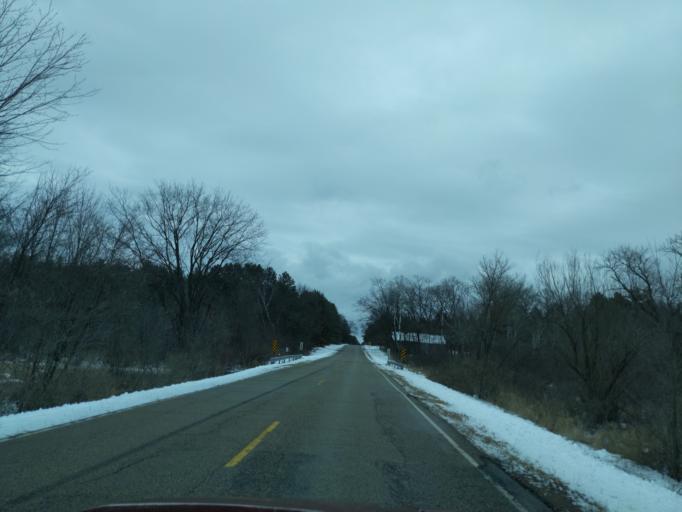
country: US
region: Wisconsin
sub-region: Marquette County
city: Montello
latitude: 43.9197
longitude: -89.3190
